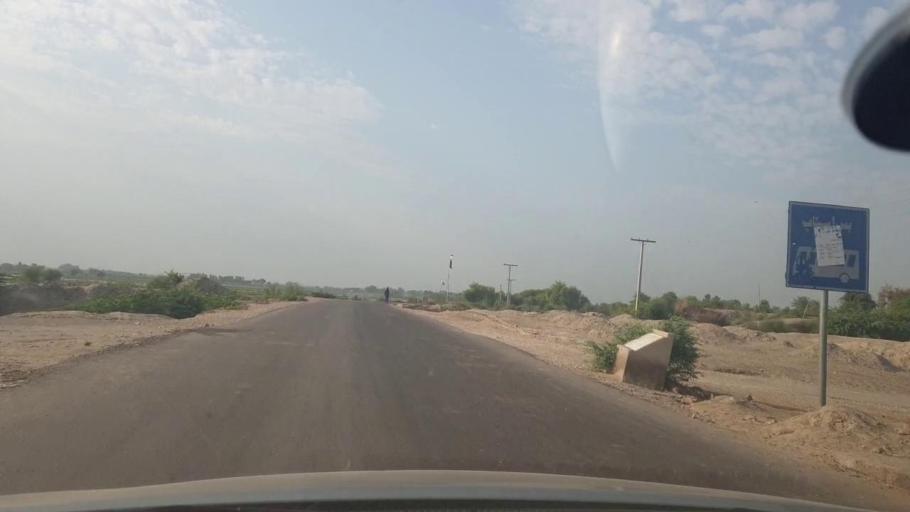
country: PK
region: Sindh
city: Jacobabad
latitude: 28.1253
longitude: 68.3283
